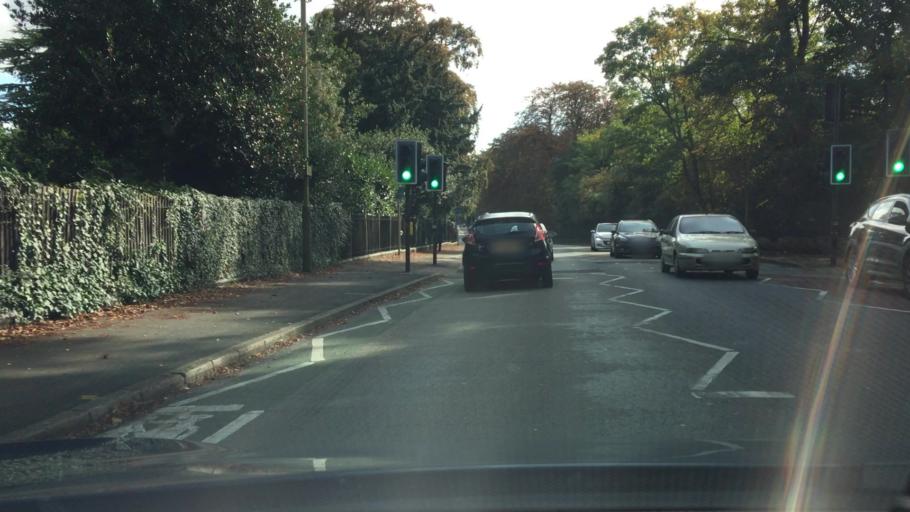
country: GB
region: England
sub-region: City of Leicester
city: Leicester
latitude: 52.6203
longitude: -1.1115
